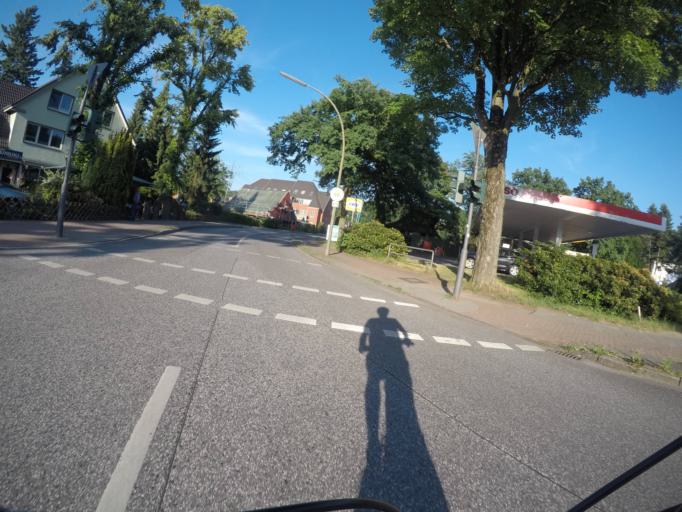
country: DE
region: Schleswig-Holstein
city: Wedel
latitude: 53.5813
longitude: 9.7632
